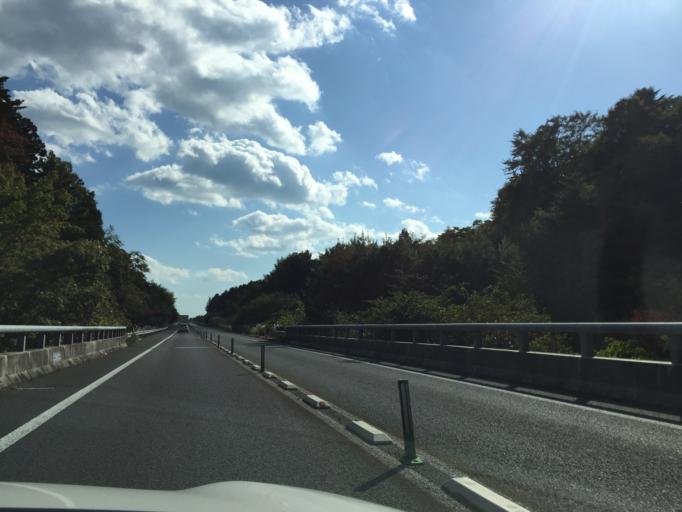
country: JP
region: Fukushima
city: Iwaki
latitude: 37.2123
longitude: 140.9802
